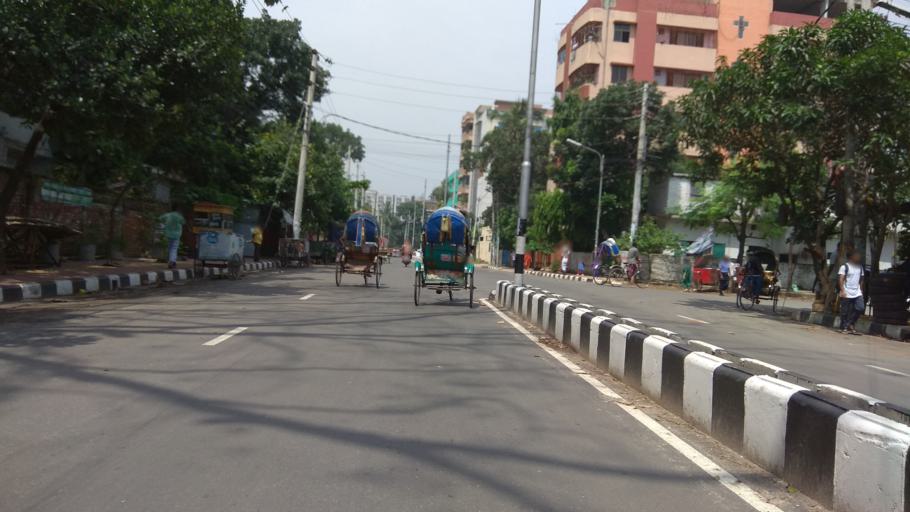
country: BD
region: Dhaka
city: Azimpur
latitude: 23.8037
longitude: 90.3591
